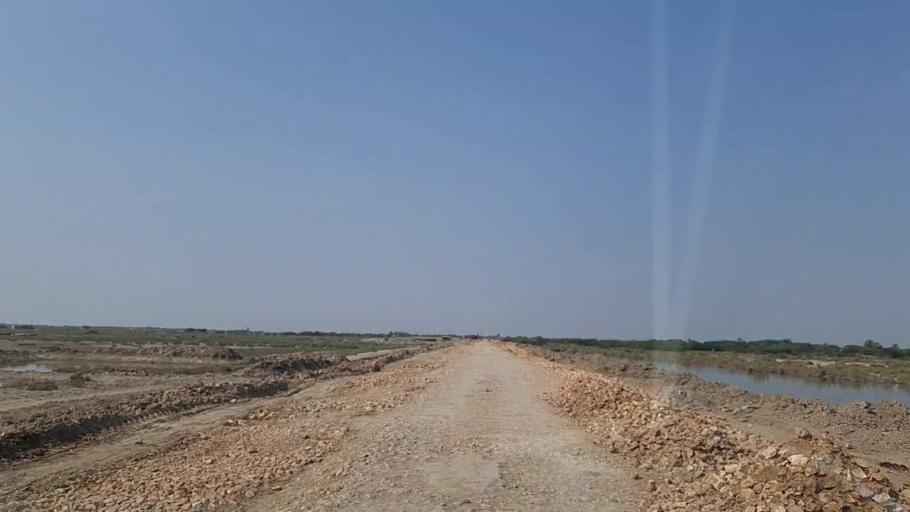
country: PK
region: Sindh
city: Chuhar Jamali
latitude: 24.1934
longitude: 67.8400
